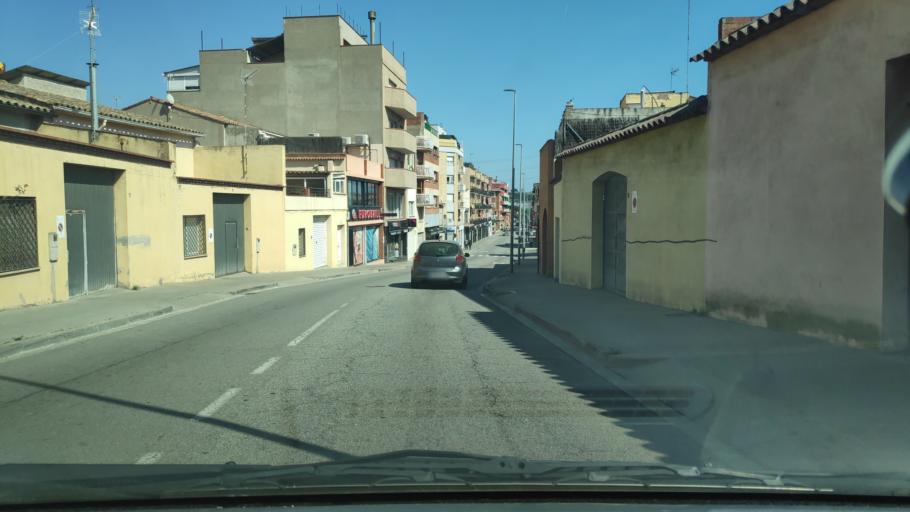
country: ES
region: Catalonia
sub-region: Provincia de Barcelona
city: Santa Perpetua de Mogoda
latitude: 41.5359
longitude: 2.1778
